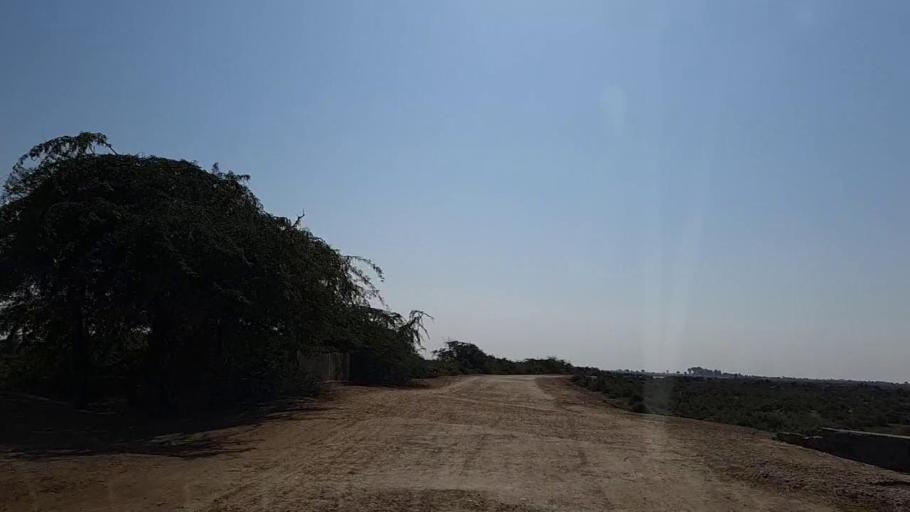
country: PK
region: Sindh
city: Chuhar Jamali
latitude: 24.5119
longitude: 68.0973
